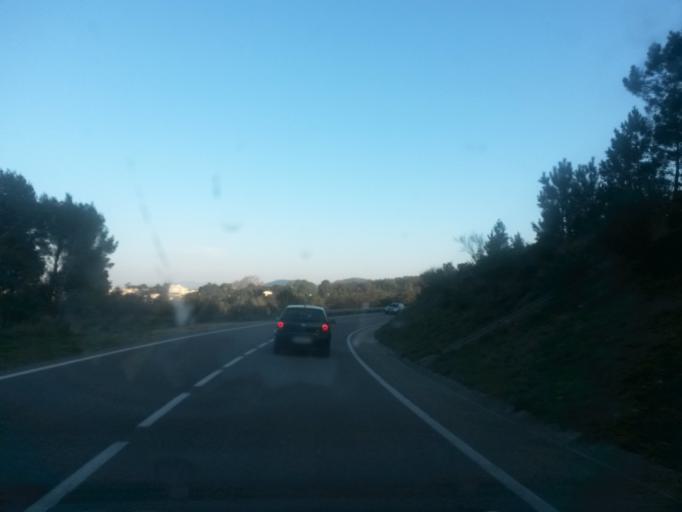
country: ES
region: Catalonia
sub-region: Provincia de Girona
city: Darnius
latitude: 42.3678
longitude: 2.8247
